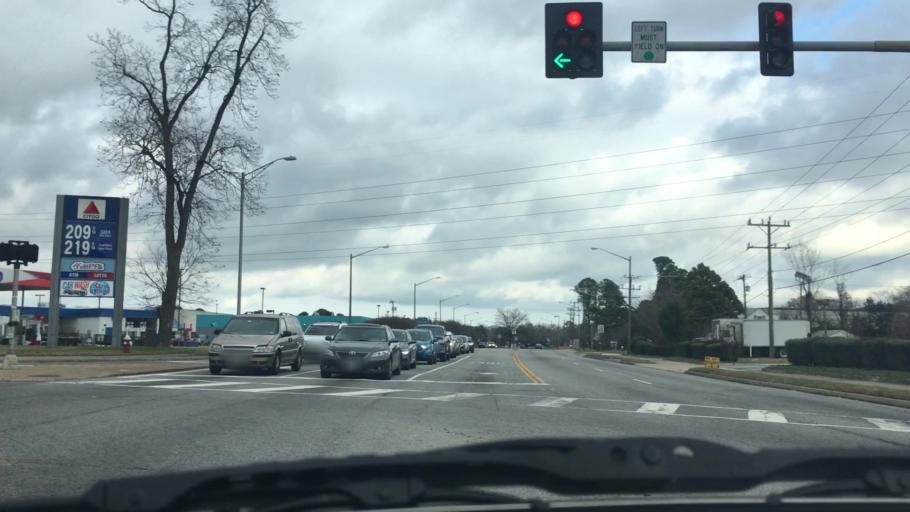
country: US
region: Virginia
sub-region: City of Chesapeake
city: Chesapeake
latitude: 36.8596
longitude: -76.1753
